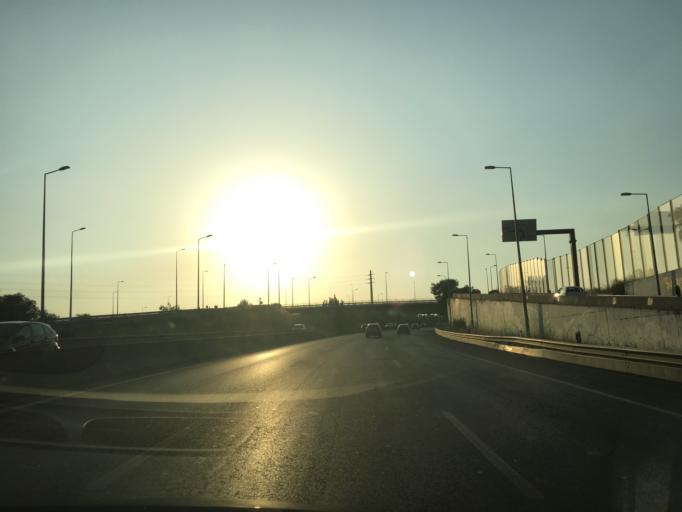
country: PT
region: Lisbon
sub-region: Sintra
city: Cacem
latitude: 38.7669
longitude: -9.3132
